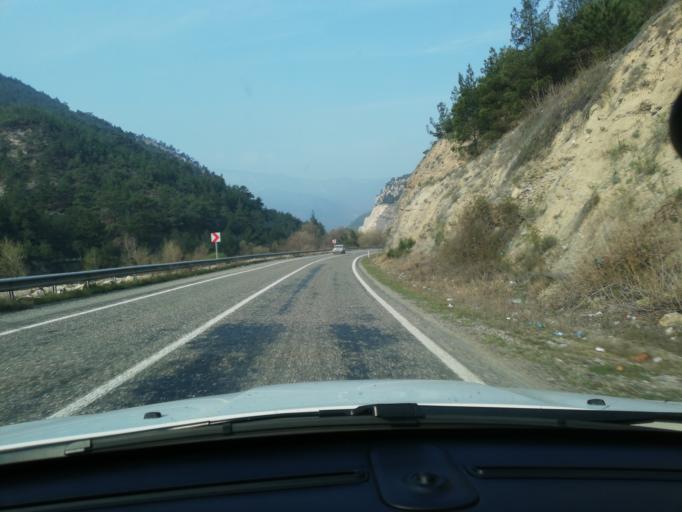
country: TR
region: Karabuk
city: Karabuk
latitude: 41.1602
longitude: 32.5594
